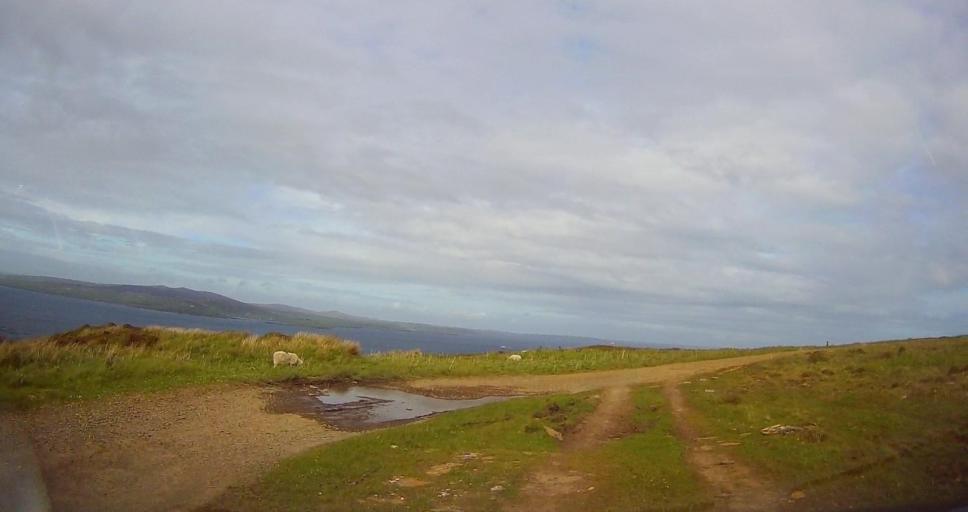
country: GB
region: Scotland
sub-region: Orkney Islands
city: Stromness
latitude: 58.8792
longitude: -3.2436
